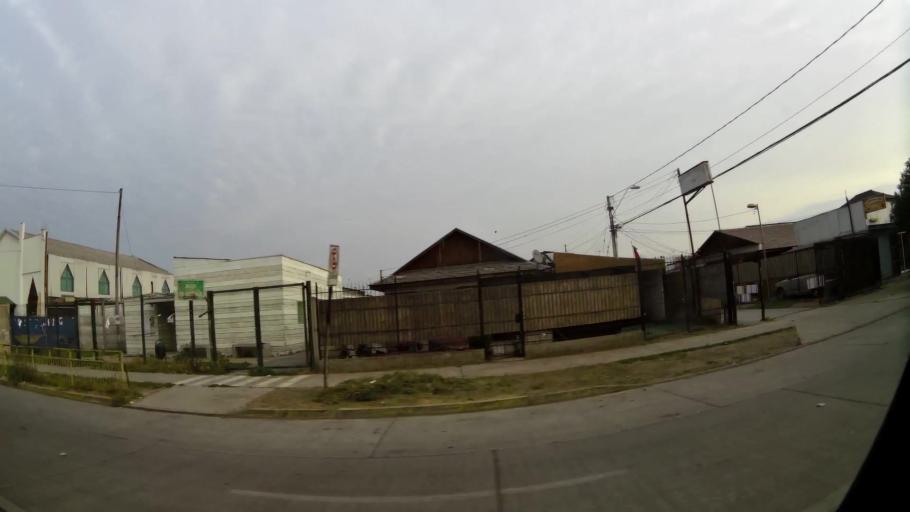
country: CL
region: Santiago Metropolitan
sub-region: Provincia de Santiago
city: Lo Prado
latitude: -33.5223
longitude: -70.7957
